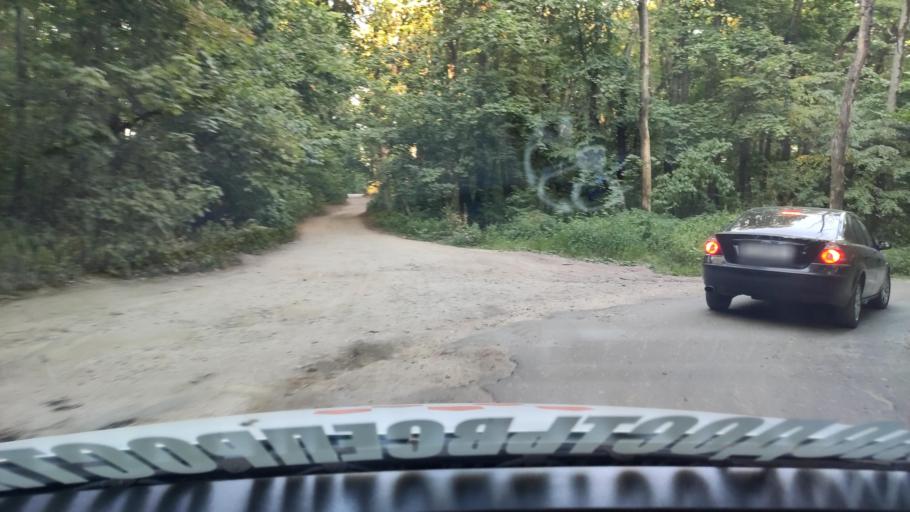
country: RU
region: Voronezj
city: Podgornoye
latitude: 51.7431
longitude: 39.2232
